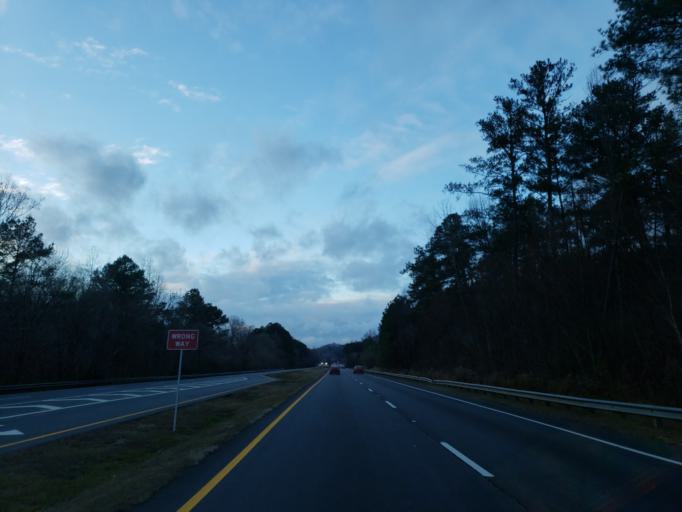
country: US
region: Georgia
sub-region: Fulton County
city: Union City
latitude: 33.6645
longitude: -84.5413
